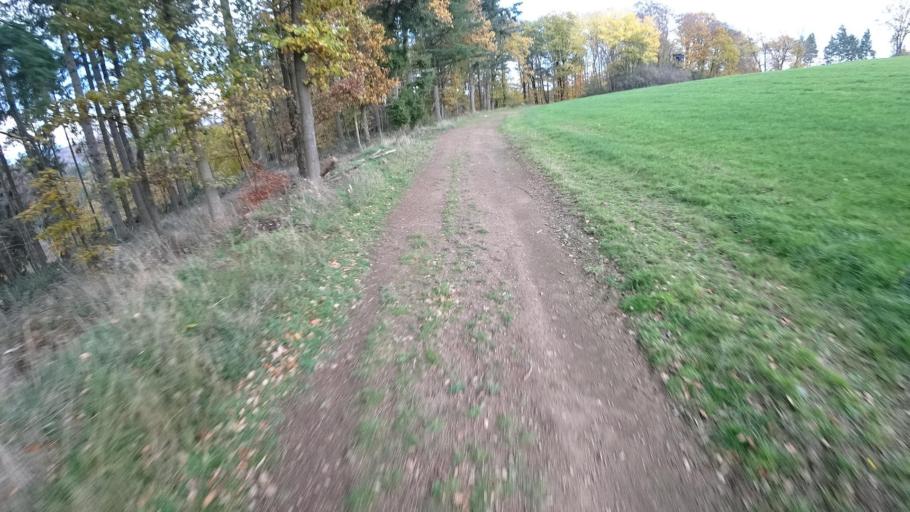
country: DE
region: Rheinland-Pfalz
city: Harscheid
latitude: 50.4658
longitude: 6.8957
